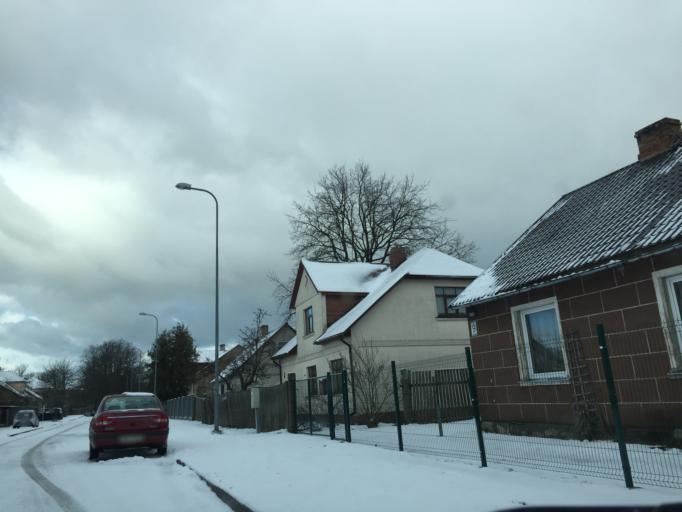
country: LV
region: Ventspils
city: Ventspils
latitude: 57.3849
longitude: 21.5645
